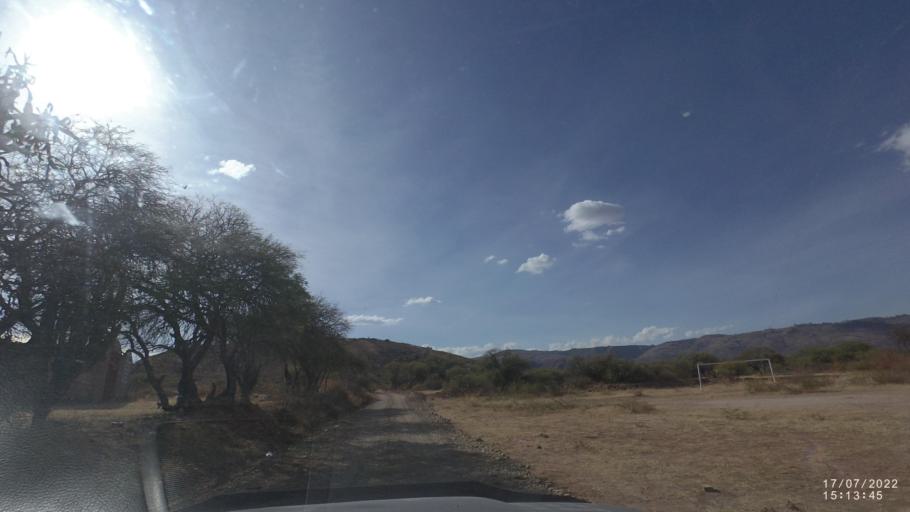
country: BO
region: Cochabamba
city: Capinota
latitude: -17.5656
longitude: -66.2627
